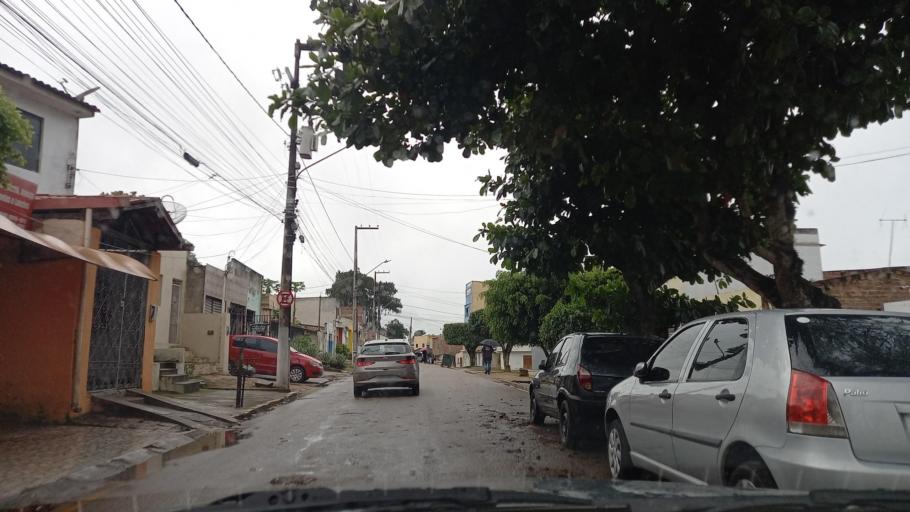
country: BR
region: Pernambuco
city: Garanhuns
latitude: -8.8867
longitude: -36.5005
